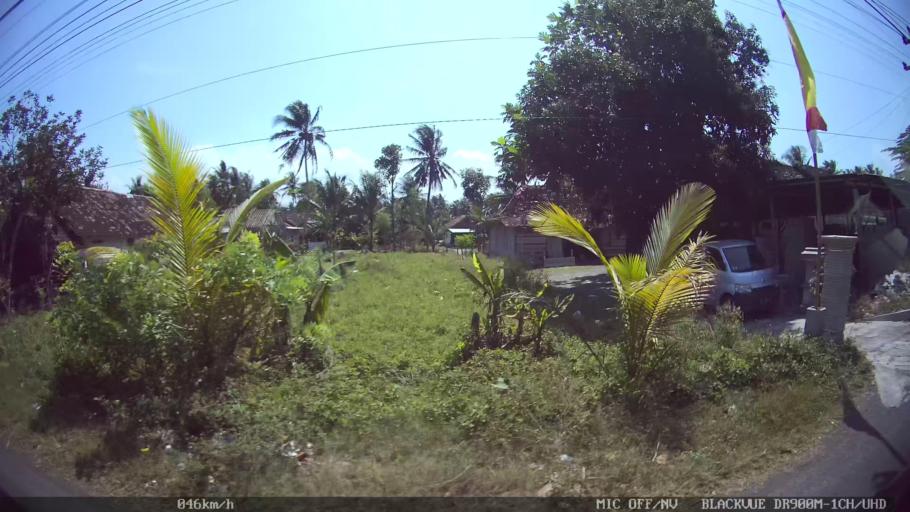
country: ID
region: Daerah Istimewa Yogyakarta
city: Srandakan
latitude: -7.9095
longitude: 110.0856
